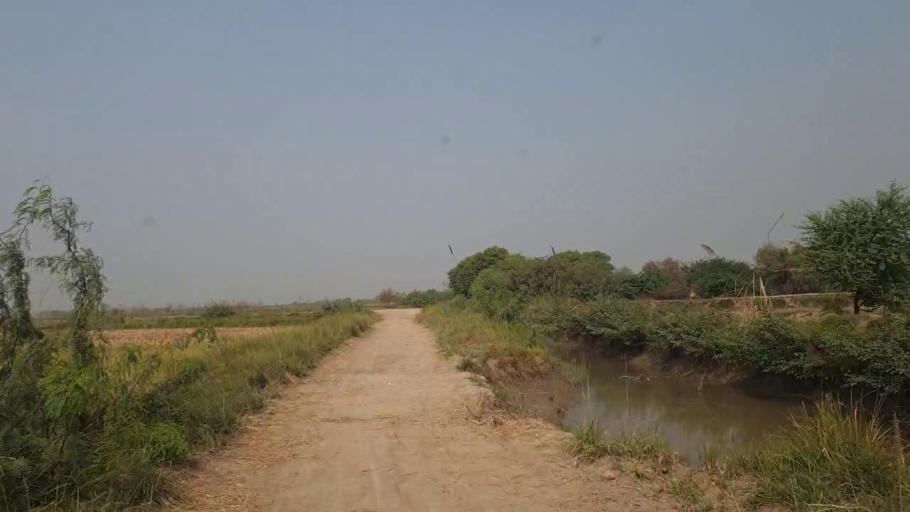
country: PK
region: Sindh
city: Matli
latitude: 25.1225
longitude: 68.6533
